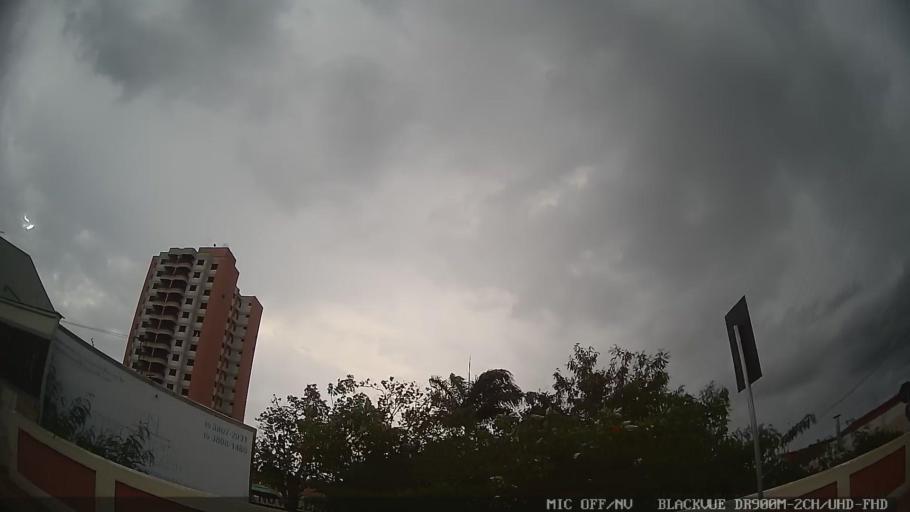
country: BR
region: Sao Paulo
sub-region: Amparo
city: Amparo
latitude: -22.7060
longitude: -46.7714
